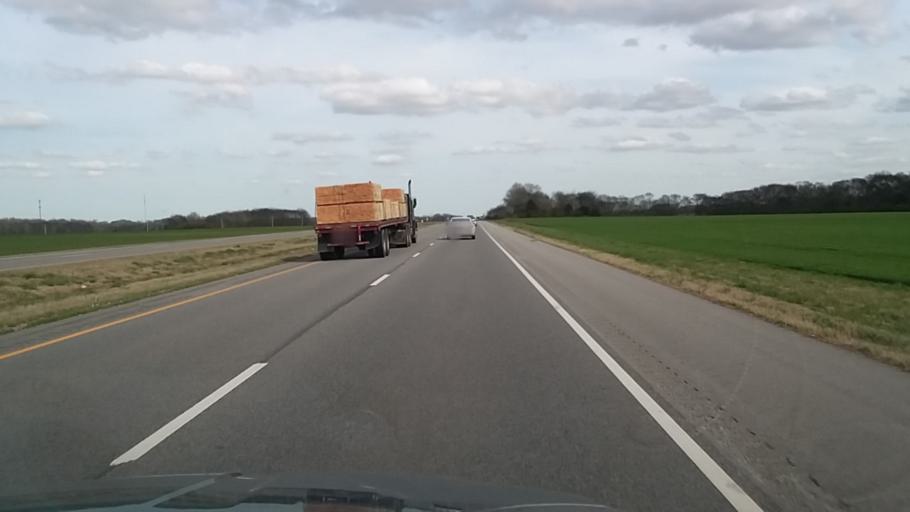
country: US
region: Alabama
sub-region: Lawrence County
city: Town Creek
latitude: 34.6840
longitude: -87.5371
